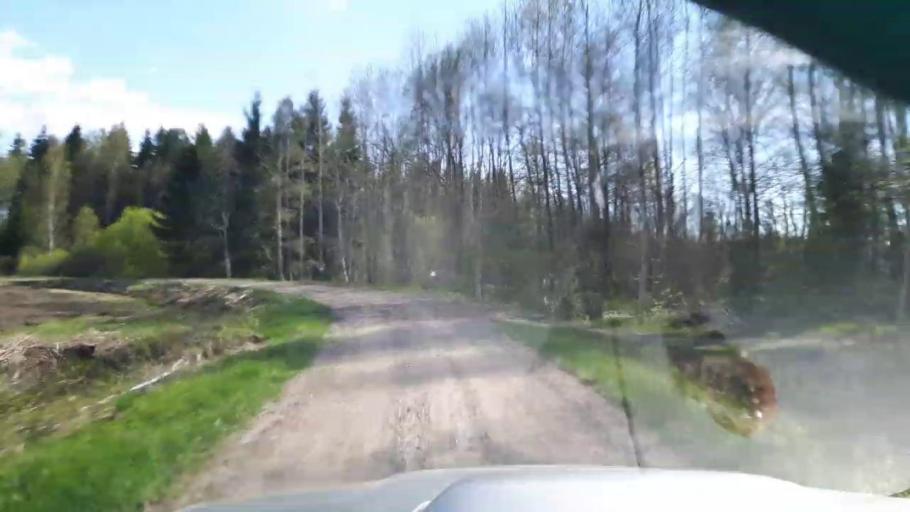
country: EE
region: Paernumaa
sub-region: Tootsi vald
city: Tootsi
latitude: 58.4496
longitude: 24.8473
